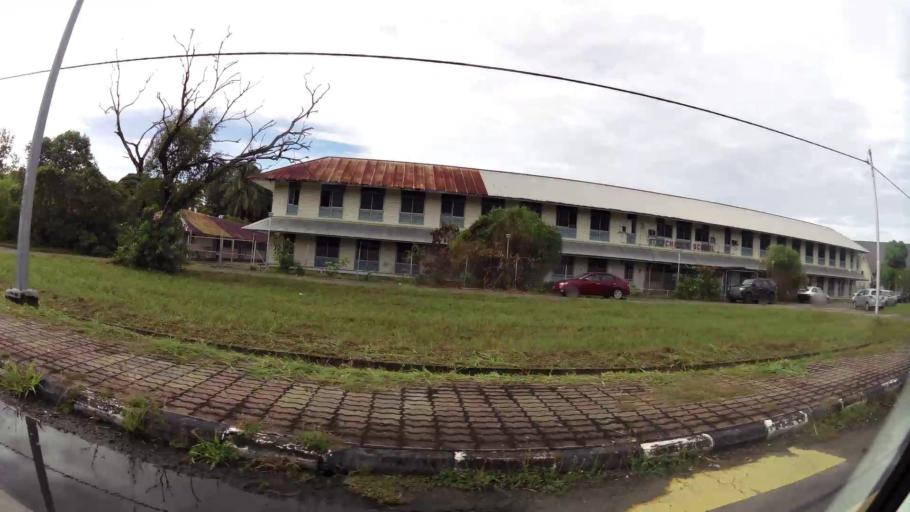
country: BN
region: Belait
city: Seria
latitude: 4.6137
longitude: 114.3360
